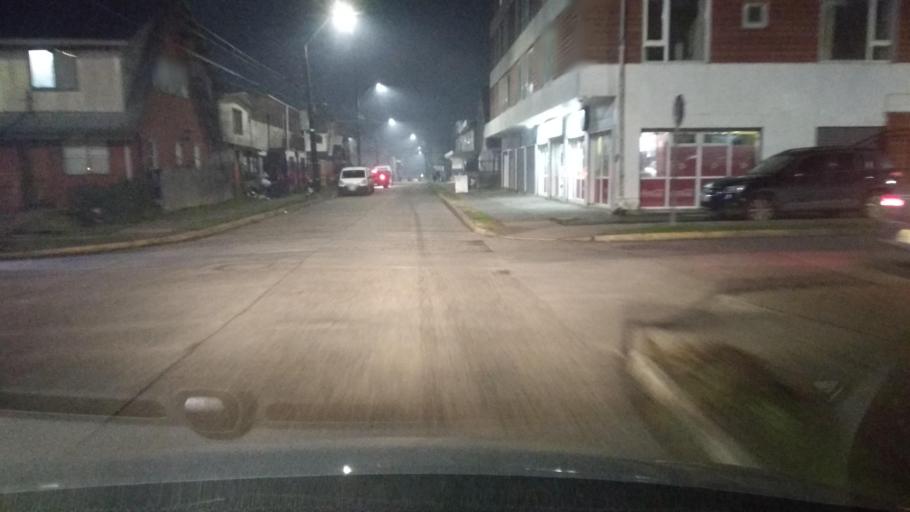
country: CL
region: Los Rios
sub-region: Provincia de Valdivia
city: Valdivia
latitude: -39.8150
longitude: -73.2570
